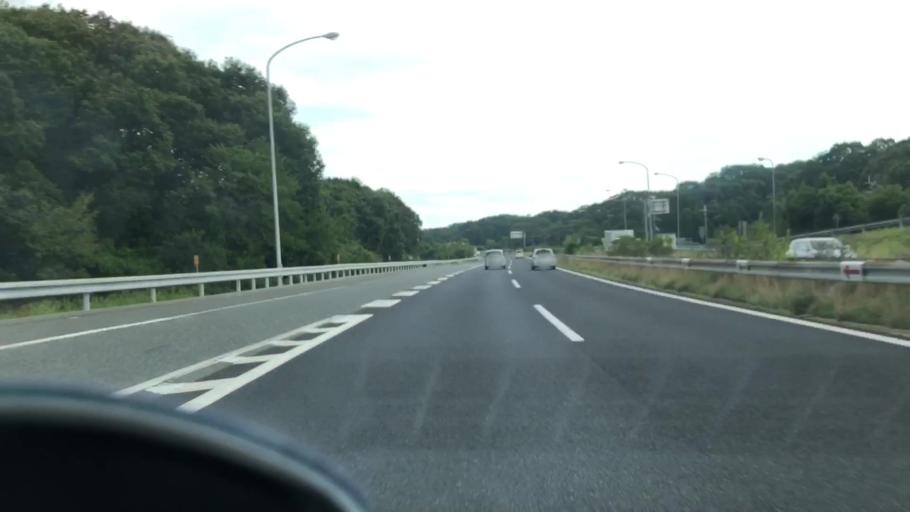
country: JP
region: Hyogo
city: Yashiro
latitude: 34.8956
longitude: 135.0803
